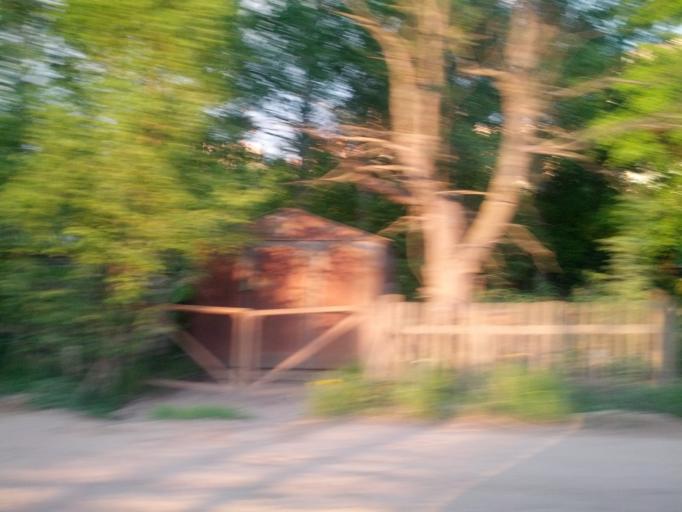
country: RU
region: Leningrad
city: Rybatskoye
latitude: 59.9057
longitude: 30.5061
